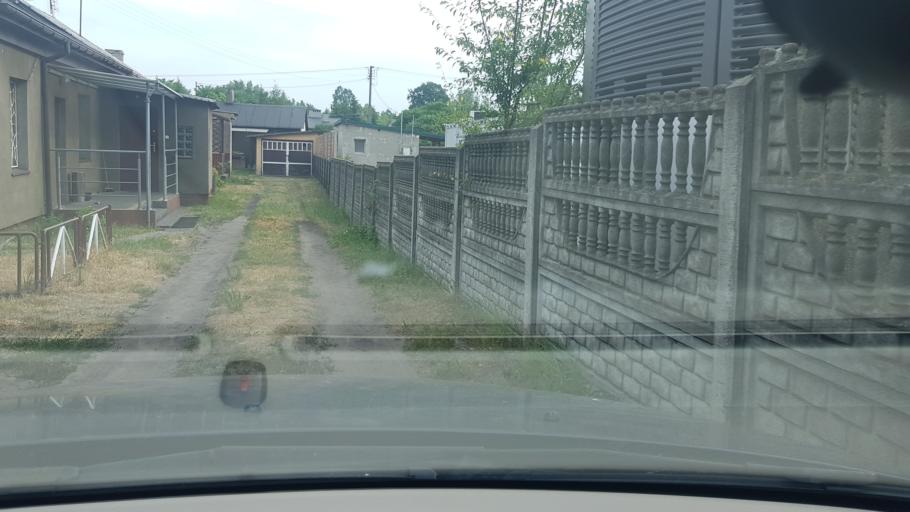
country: PL
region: Lodz Voivodeship
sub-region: Powiat tomaszowski
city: Tomaszow Mazowiecki
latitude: 51.5521
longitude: 20.0243
